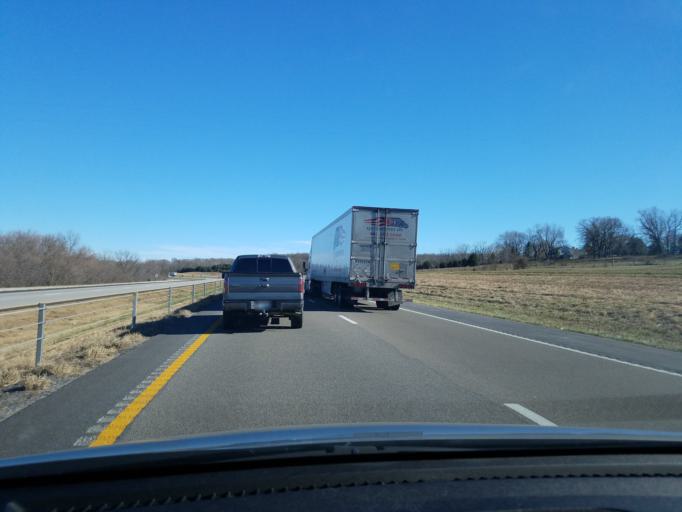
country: US
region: Missouri
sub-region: Webster County
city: Marshfield
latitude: 37.3027
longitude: -92.9898
